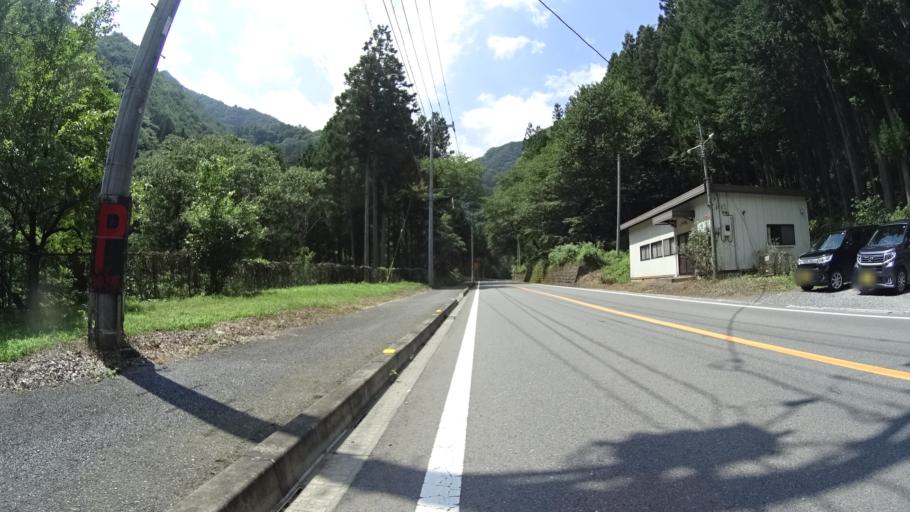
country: JP
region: Gunma
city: Tomioka
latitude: 36.0783
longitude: 138.7829
